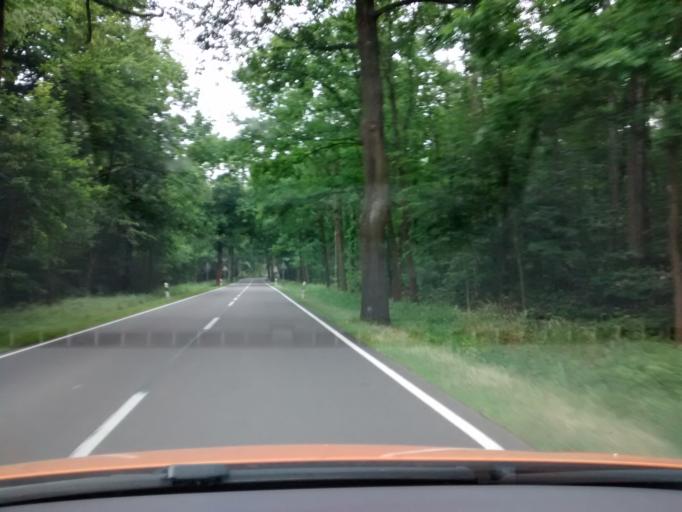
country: DE
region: Brandenburg
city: Wiesenburg
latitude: 52.0908
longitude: 12.4411
